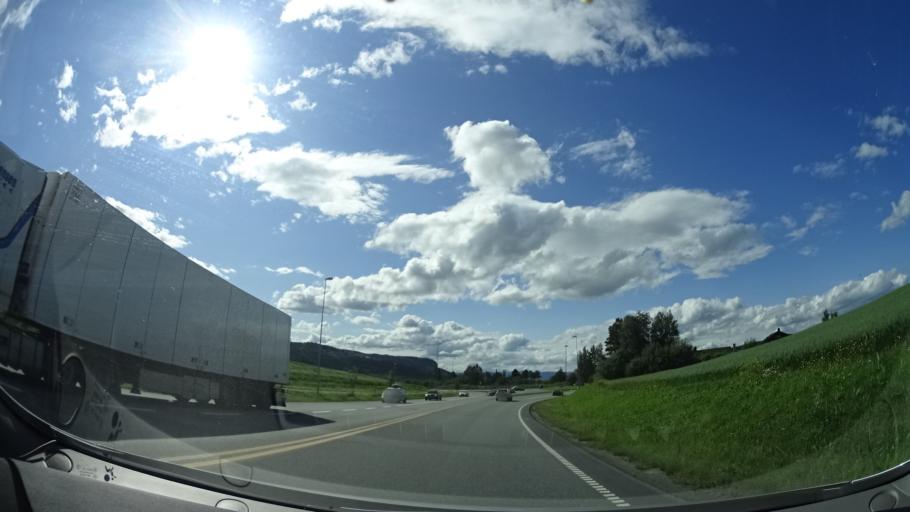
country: NO
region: Sor-Trondelag
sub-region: Melhus
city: Melhus
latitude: 63.3224
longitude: 10.3086
